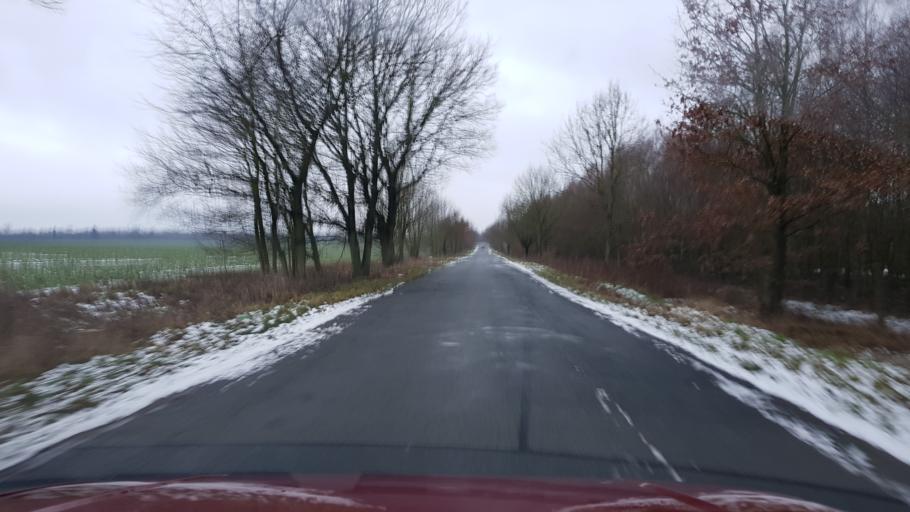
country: PL
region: West Pomeranian Voivodeship
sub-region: Powiat gryficki
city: Ploty
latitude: 53.6874
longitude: 15.2444
